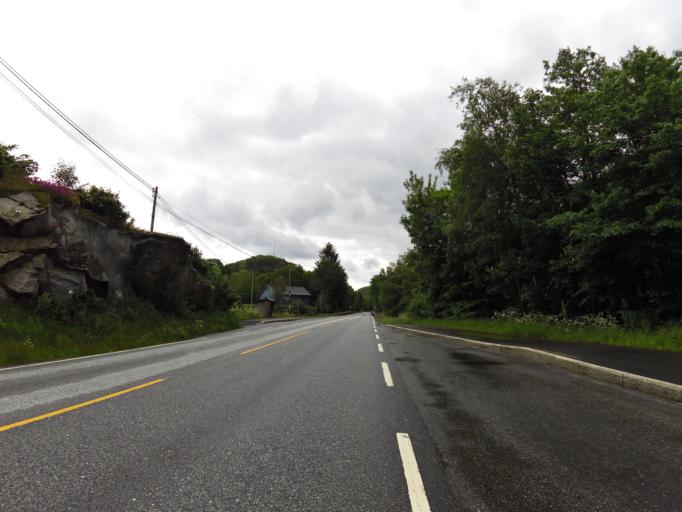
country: NO
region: Vest-Agder
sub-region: Farsund
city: Farsund
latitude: 58.1007
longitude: 6.8683
